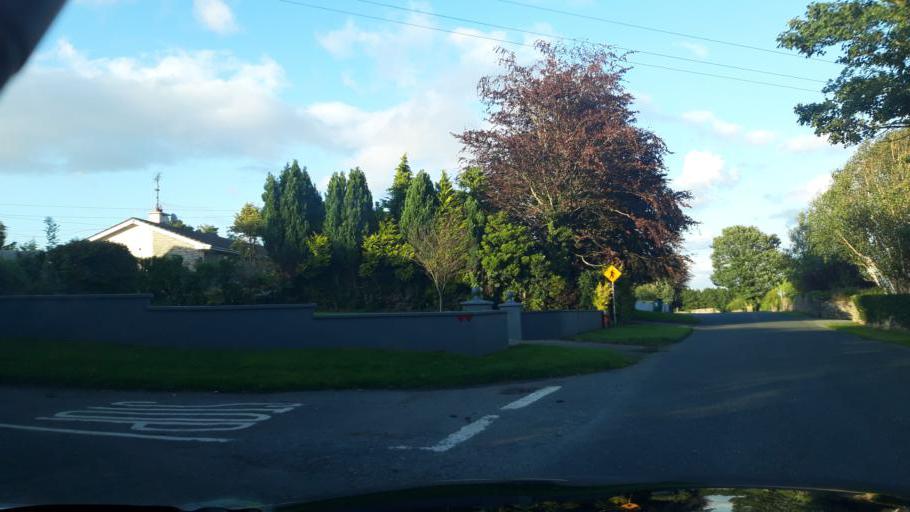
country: IE
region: Leinster
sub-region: An Iarmhi
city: Athlone
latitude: 53.4248
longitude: -7.8822
